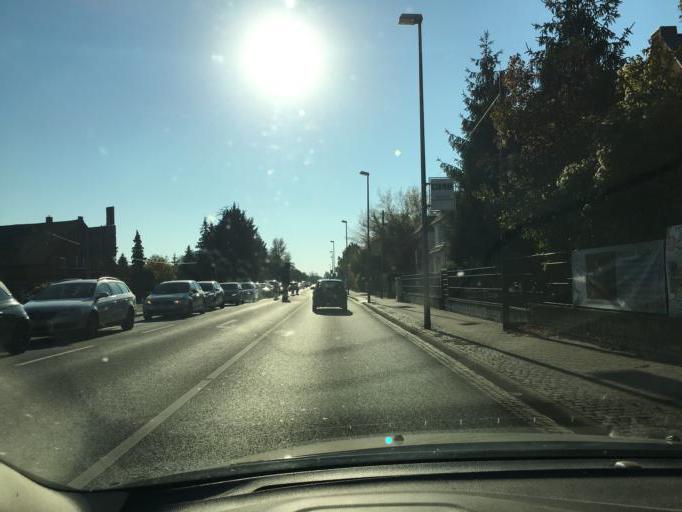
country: DE
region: Saxony-Anhalt
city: Holzweissig
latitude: 51.6088
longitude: 12.3001
